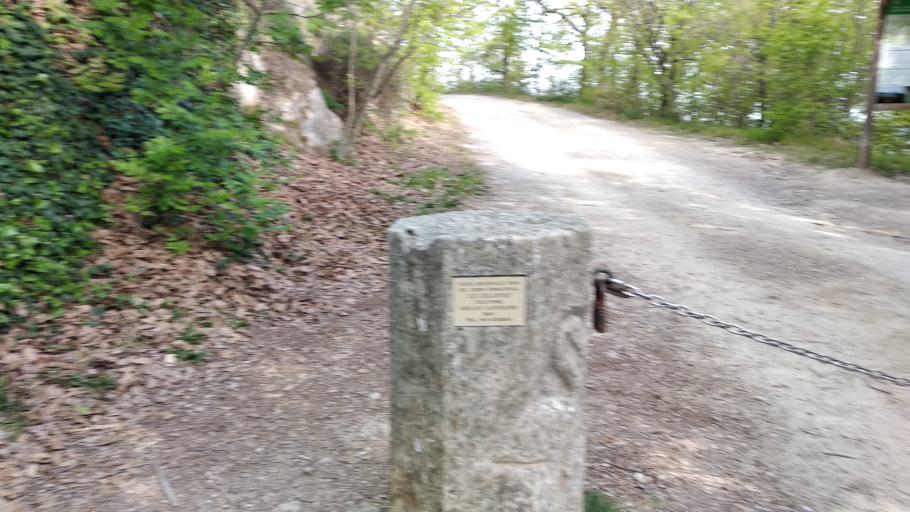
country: IT
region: Emilia-Romagna
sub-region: Provincia di Ravenna
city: Fognano
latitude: 44.2270
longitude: 11.7427
